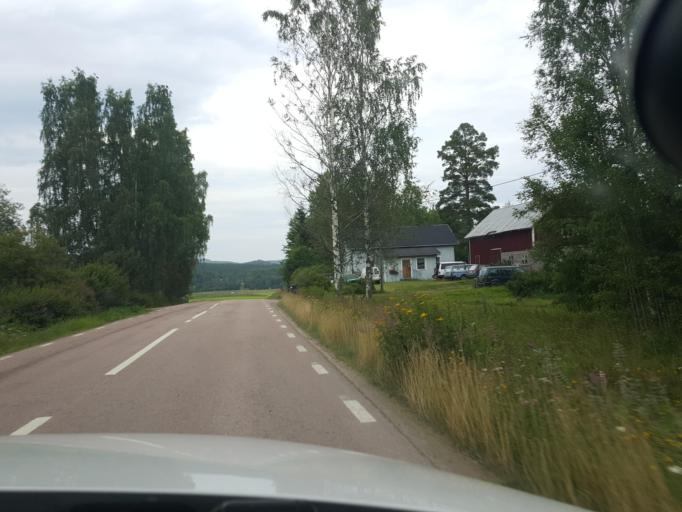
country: SE
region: Gaevleborg
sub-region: Hudiksvalls Kommun
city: Delsbo
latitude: 61.9535
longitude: 16.4797
